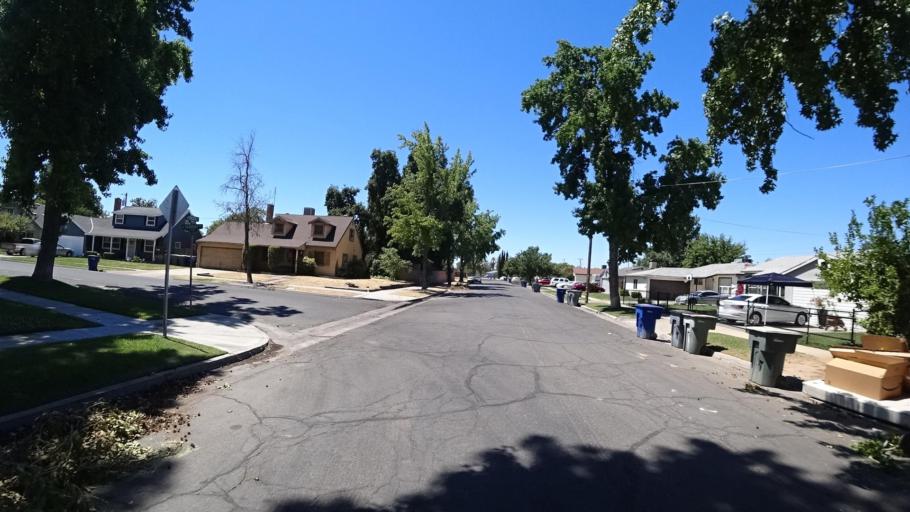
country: US
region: California
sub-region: Fresno County
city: Fresno
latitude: 36.8066
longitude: -119.7836
